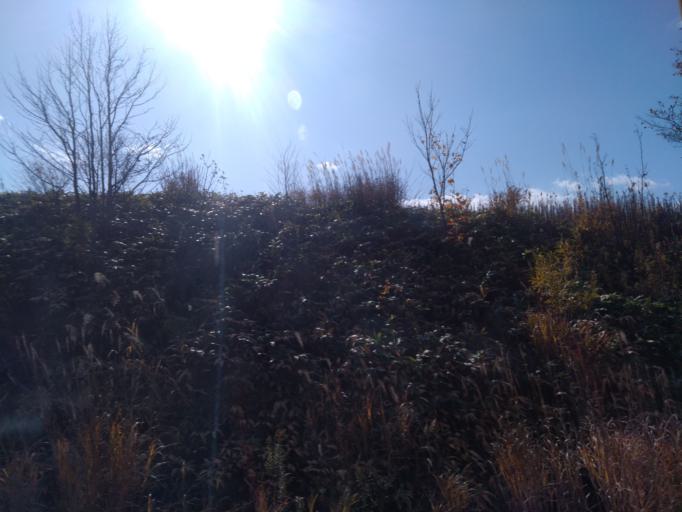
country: JP
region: Hokkaido
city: Kitahiroshima
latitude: 43.0068
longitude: 141.5023
